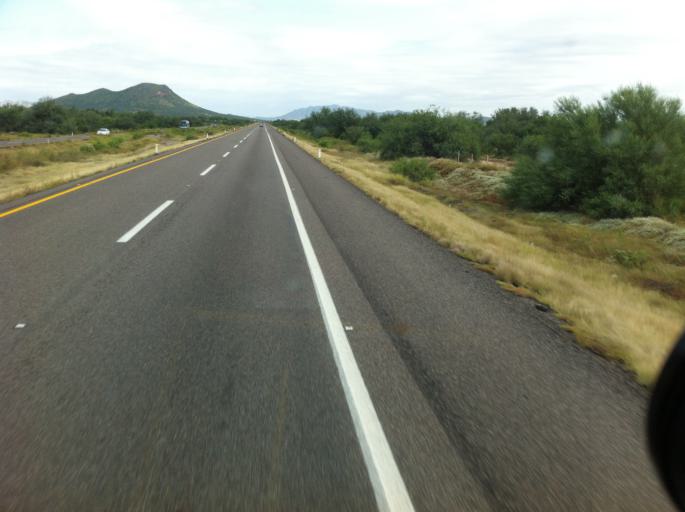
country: MX
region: Sonora
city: Hermosillo
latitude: 28.8526
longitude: -110.9583
